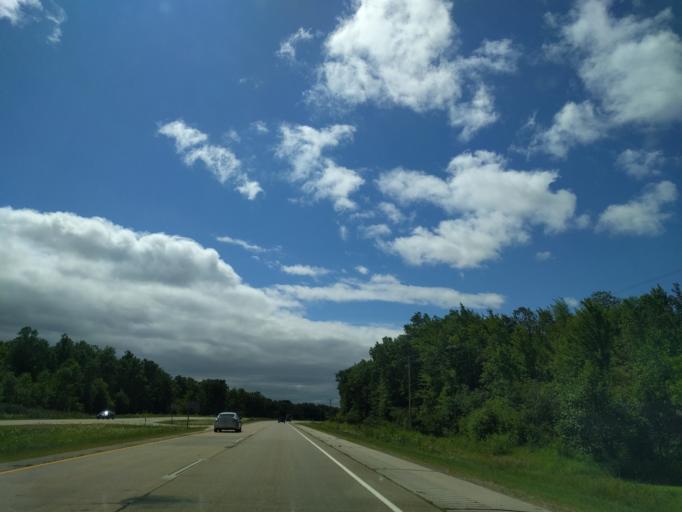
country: US
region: Wisconsin
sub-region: Oconto County
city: Oconto
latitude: 44.8568
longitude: -87.8994
